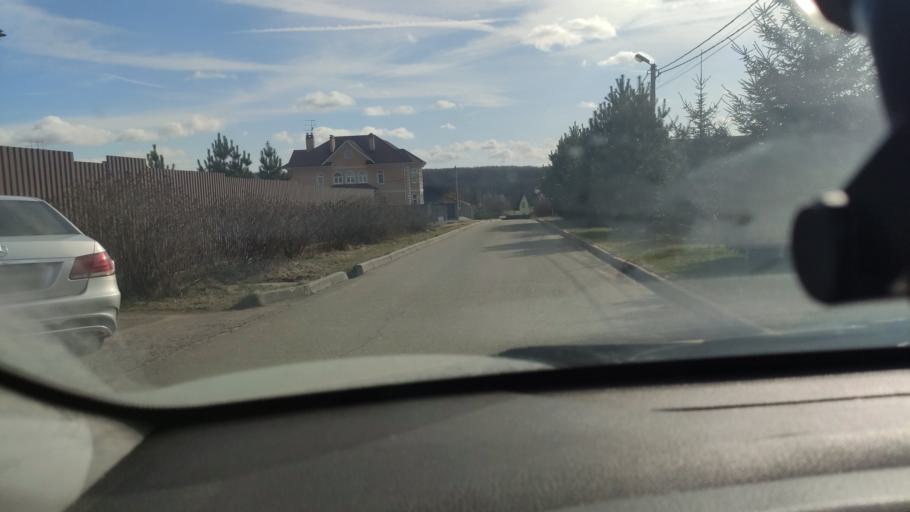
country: RU
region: Moskovskaya
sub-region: Podol'skiy Rayon
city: Podol'sk
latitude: 55.3933
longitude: 37.6257
